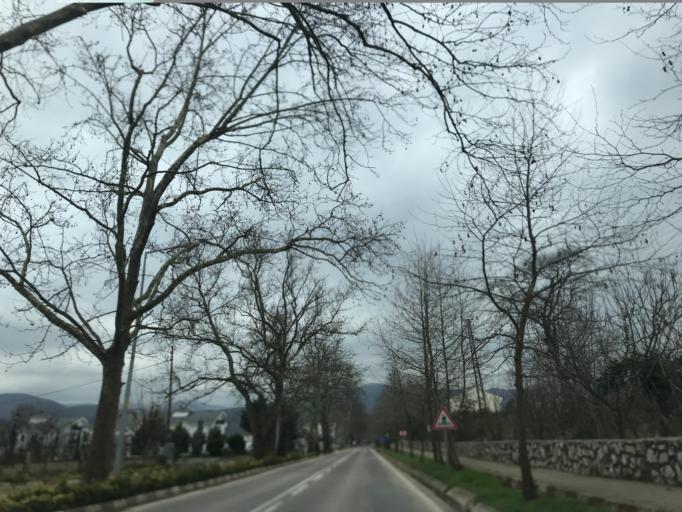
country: TR
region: Yalova
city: Kadikoy
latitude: 40.6231
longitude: 29.2199
